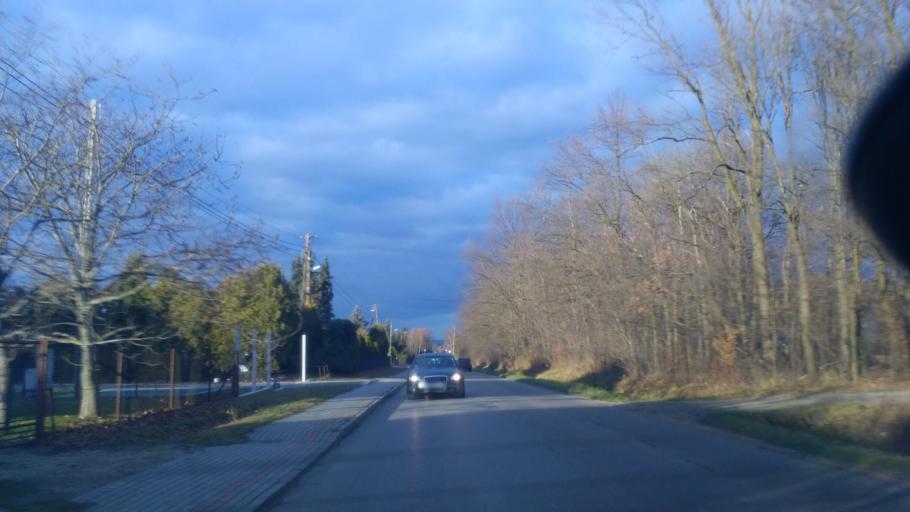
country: PL
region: Subcarpathian Voivodeship
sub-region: Powiat rzeszowski
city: Krasne
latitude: 50.0498
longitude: 22.1225
